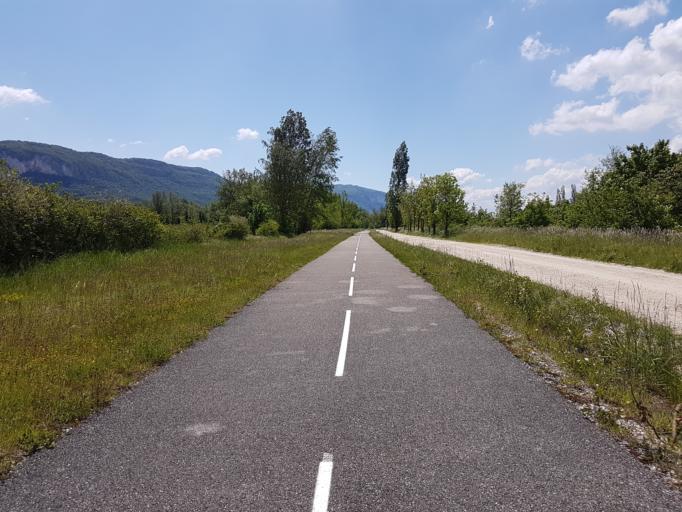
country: FR
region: Rhone-Alpes
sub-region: Departement de l'Ain
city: Belley
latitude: 45.7139
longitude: 5.7009
